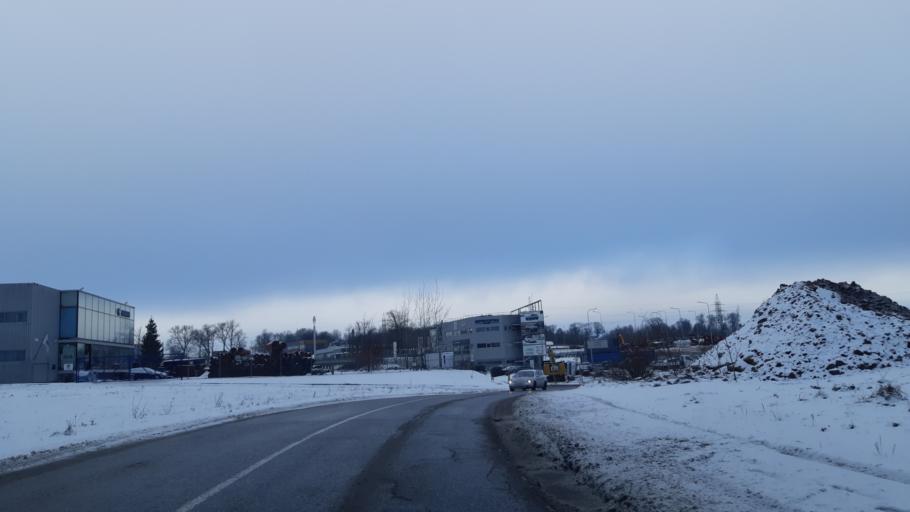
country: LT
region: Kauno apskritis
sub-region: Kaunas
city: Silainiai
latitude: 54.9348
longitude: 23.8752
